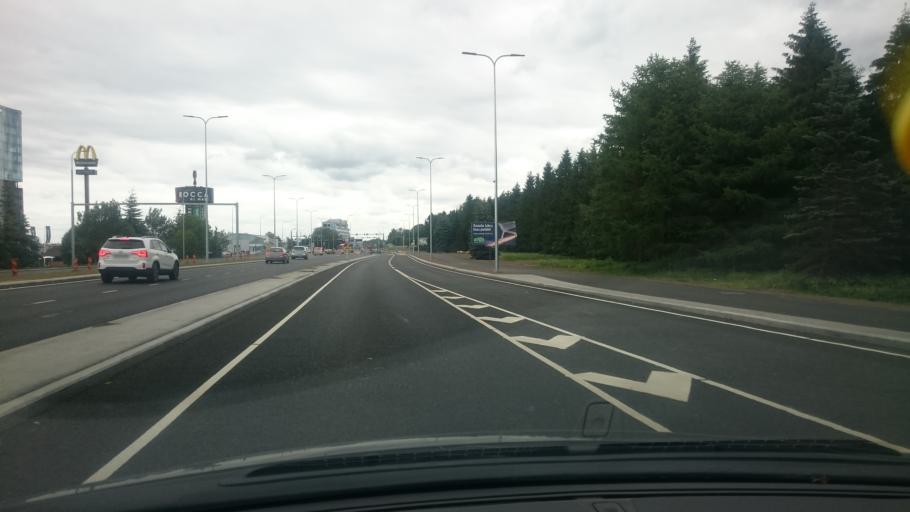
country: EE
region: Harju
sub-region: Saue vald
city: Laagri
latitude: 59.4248
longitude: 24.6525
